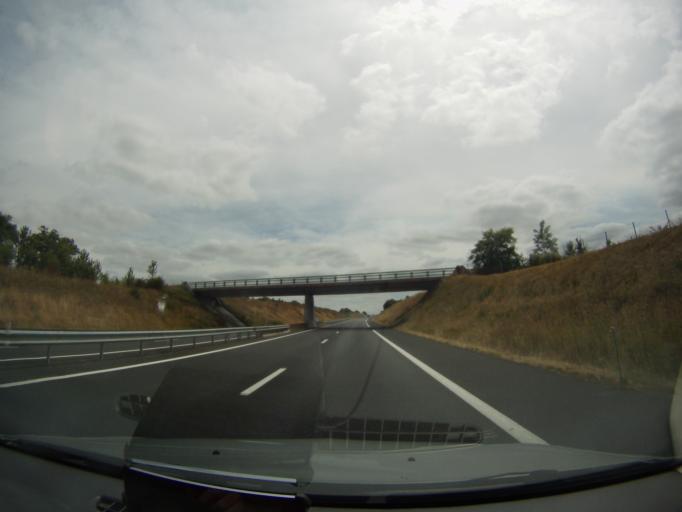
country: FR
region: Pays de la Loire
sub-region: Departement de Maine-et-Loire
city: La Tessoualle
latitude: 47.0139
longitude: -0.8730
